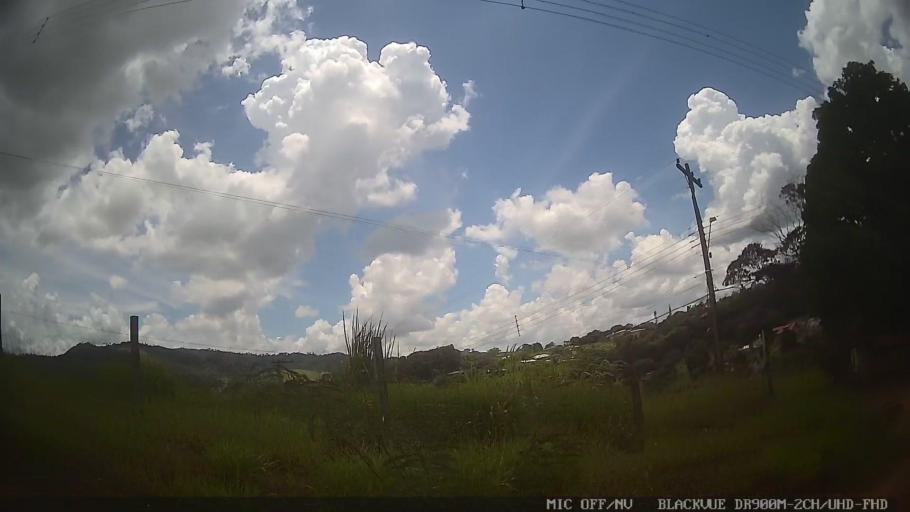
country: BR
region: Sao Paulo
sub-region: Braganca Paulista
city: Braganca Paulista
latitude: -23.0330
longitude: -46.5332
